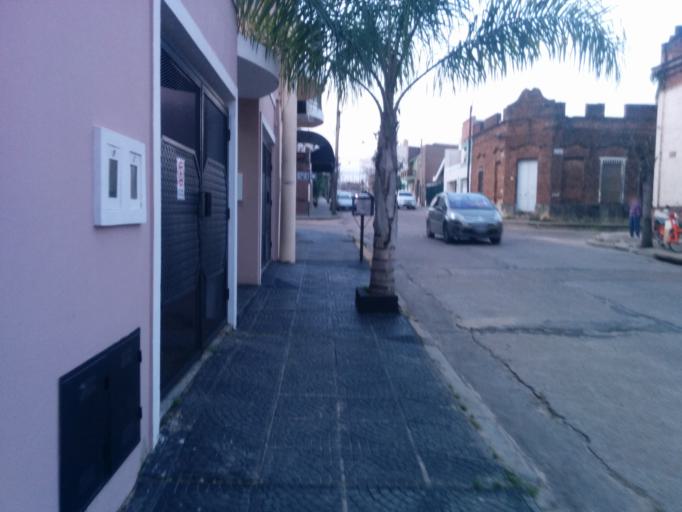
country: AR
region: Entre Rios
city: Concordia
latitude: -31.3893
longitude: -58.0213
